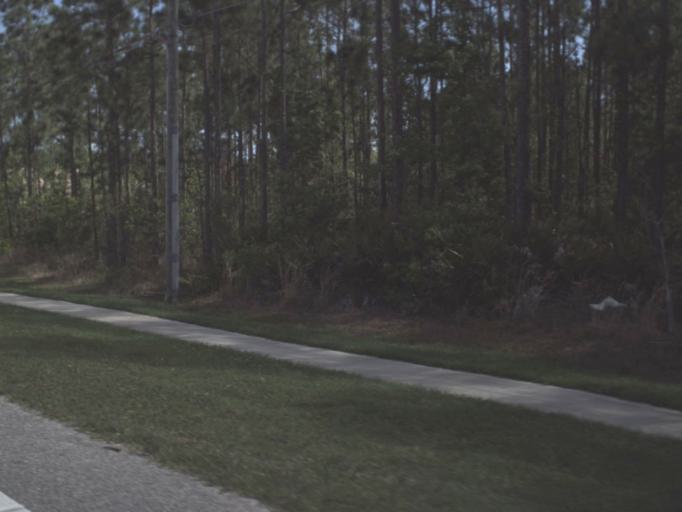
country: US
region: Florida
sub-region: Flagler County
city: Bunnell
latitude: 29.4922
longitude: -81.2652
